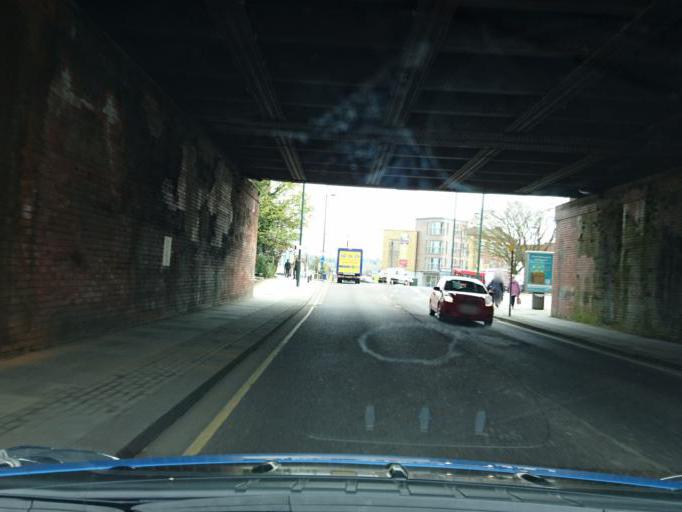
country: GB
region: England
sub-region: Greater London
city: Hadley Wood
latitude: 51.6502
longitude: -0.1738
